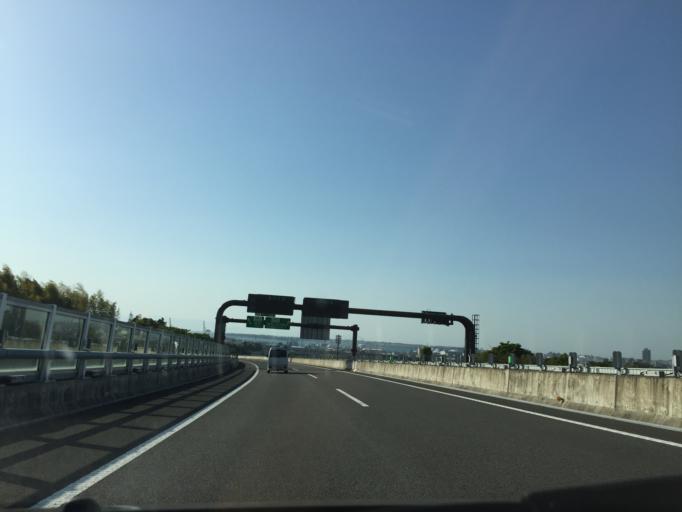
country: JP
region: Shizuoka
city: Shizuoka-shi
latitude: 35.0535
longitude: 138.4834
